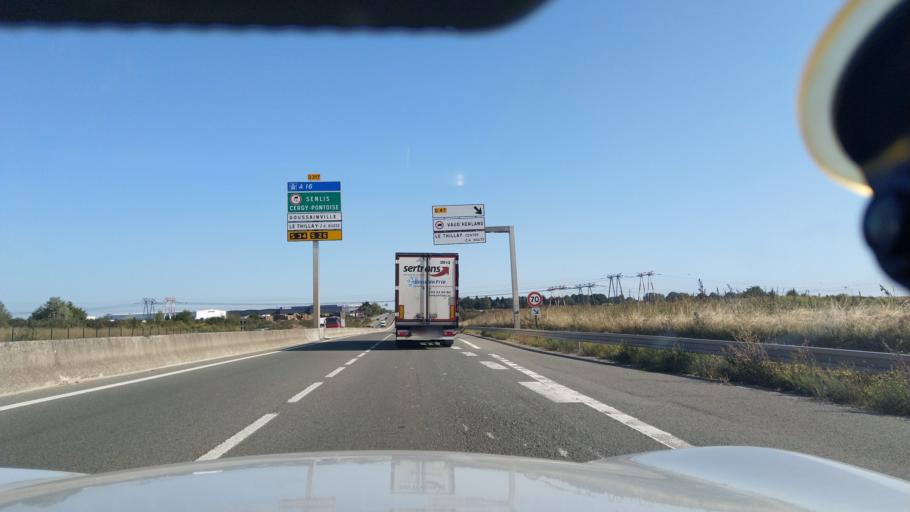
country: FR
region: Ile-de-France
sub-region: Departement du Val-d'Oise
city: Le Thillay
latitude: 48.9911
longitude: 2.4763
